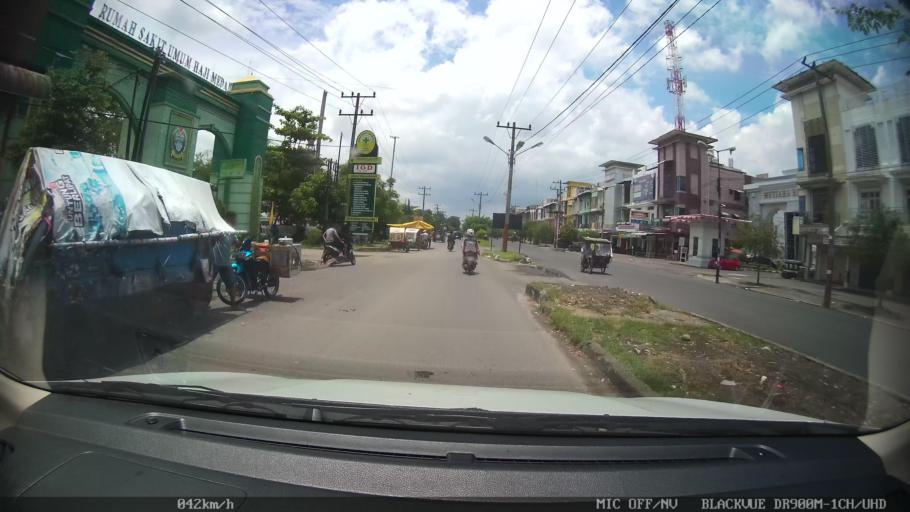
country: ID
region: North Sumatra
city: Medan
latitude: 3.6140
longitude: 98.7157
